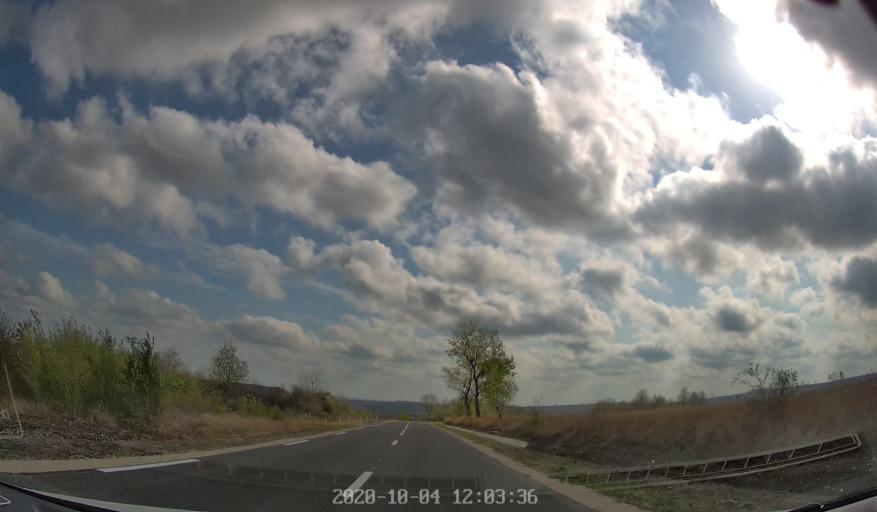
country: MD
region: Rezina
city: Saharna
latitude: 47.6108
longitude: 28.9299
